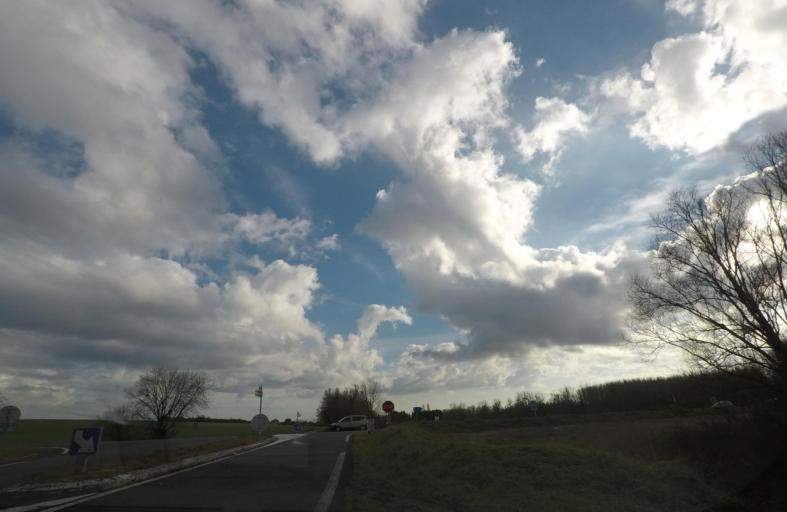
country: FR
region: Centre
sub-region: Departement du Cher
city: Bourges
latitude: 47.0462
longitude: 2.4204
